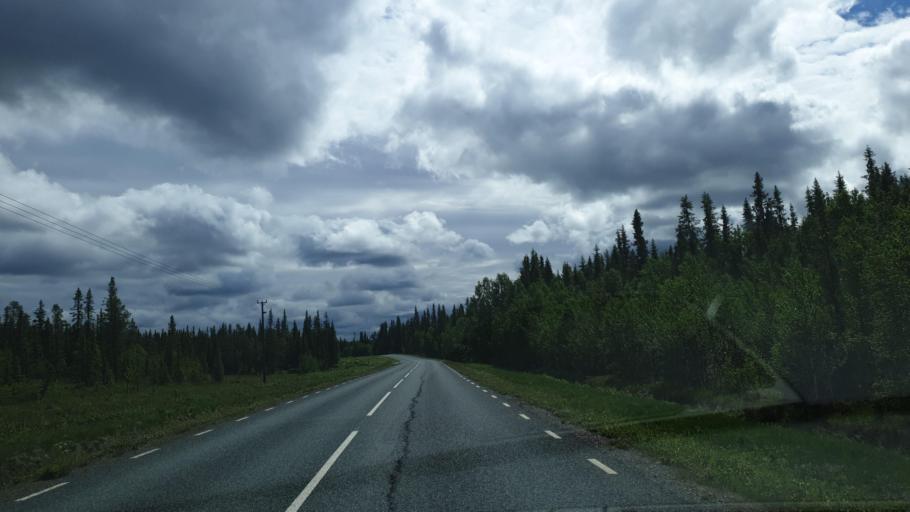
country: SE
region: Vaesterbotten
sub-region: Vilhelmina Kommun
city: Sjoberg
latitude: 65.2400
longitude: 15.7839
